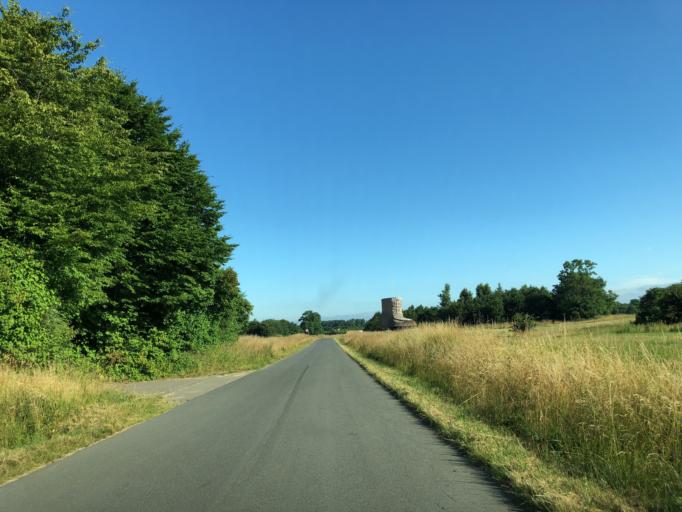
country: DK
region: South Denmark
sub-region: Sonderborg Kommune
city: Sonderborg
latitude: 54.9309
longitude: 9.7744
